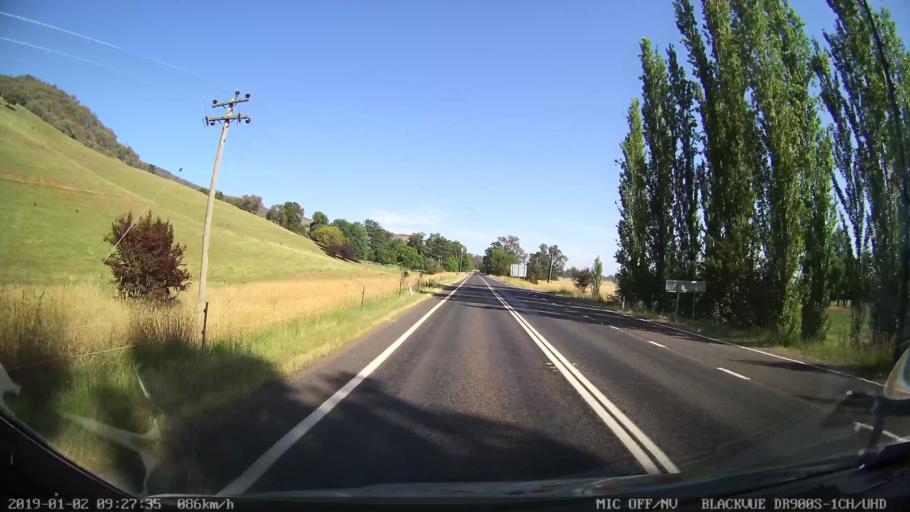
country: AU
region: New South Wales
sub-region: Tumut Shire
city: Tumut
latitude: -35.3603
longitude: 148.2564
